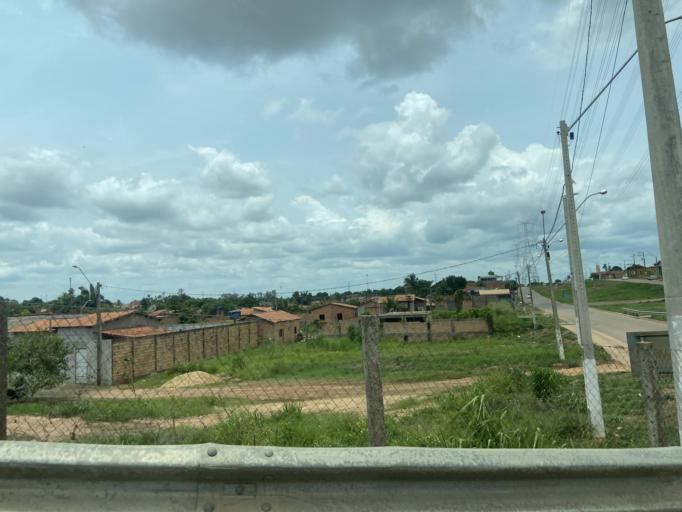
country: BR
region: Para
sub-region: Maraba
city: Maraba
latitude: -5.3488
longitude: -49.0737
